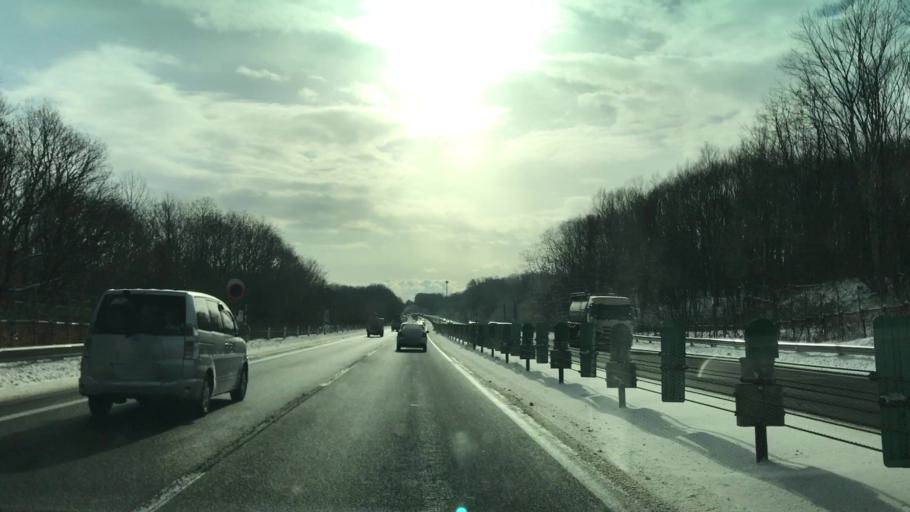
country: JP
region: Hokkaido
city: Kitahiroshima
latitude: 42.9459
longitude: 141.5174
